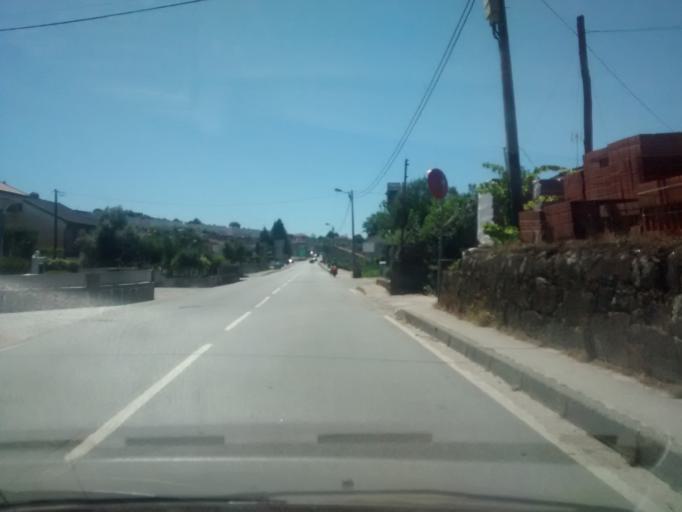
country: PT
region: Braga
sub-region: Braga
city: Oliveira
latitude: 41.5338
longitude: -8.5055
